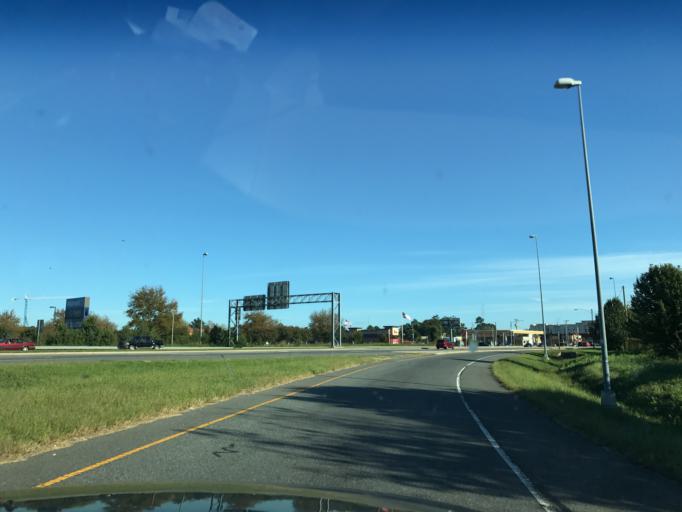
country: US
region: Virginia
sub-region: City of Chesapeake
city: Chesapeake
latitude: 36.7708
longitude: -76.2533
